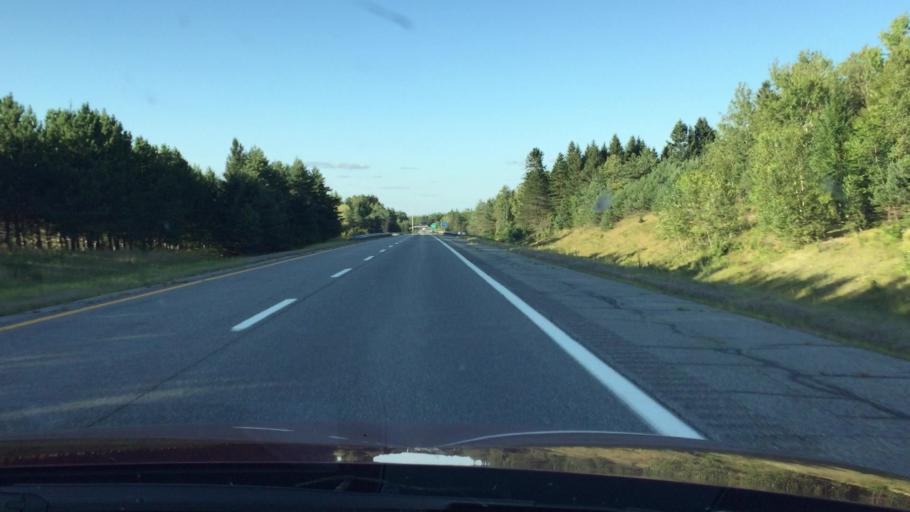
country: US
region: Maine
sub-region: Penobscot County
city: Patten
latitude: 45.8621
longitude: -68.4194
